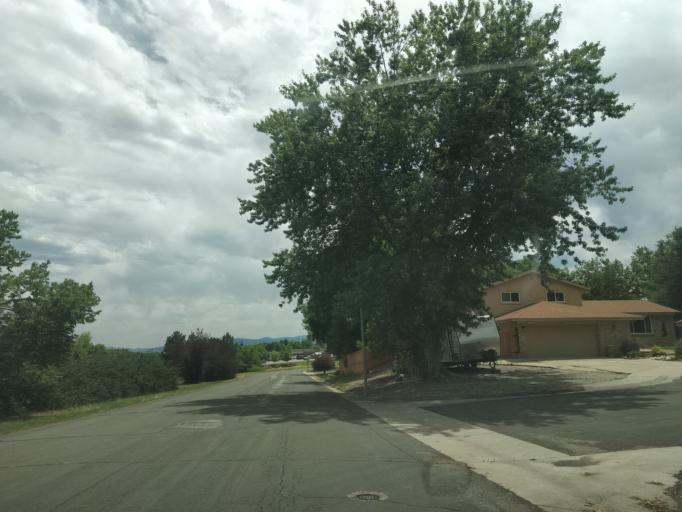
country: US
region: Colorado
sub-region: Jefferson County
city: Lakewood
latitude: 39.6837
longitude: -105.1209
